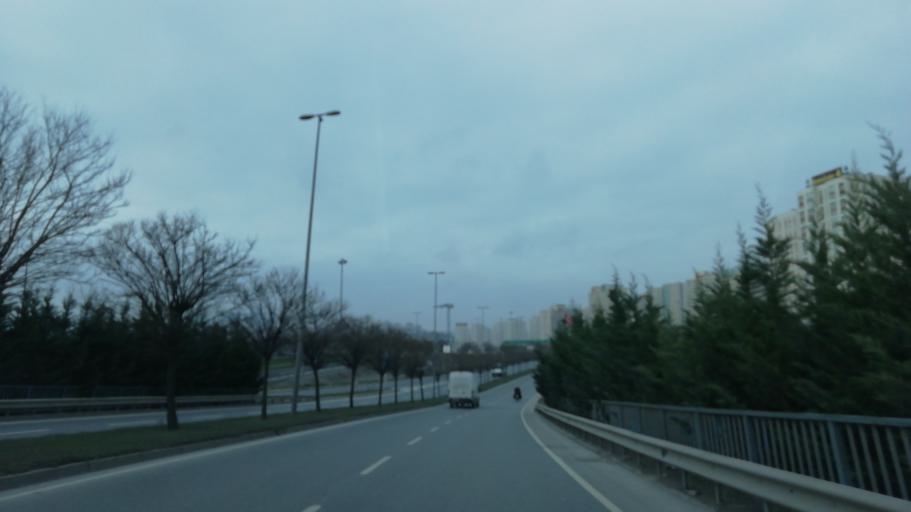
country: TR
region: Istanbul
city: Esenyurt
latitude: 41.0563
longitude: 28.7143
